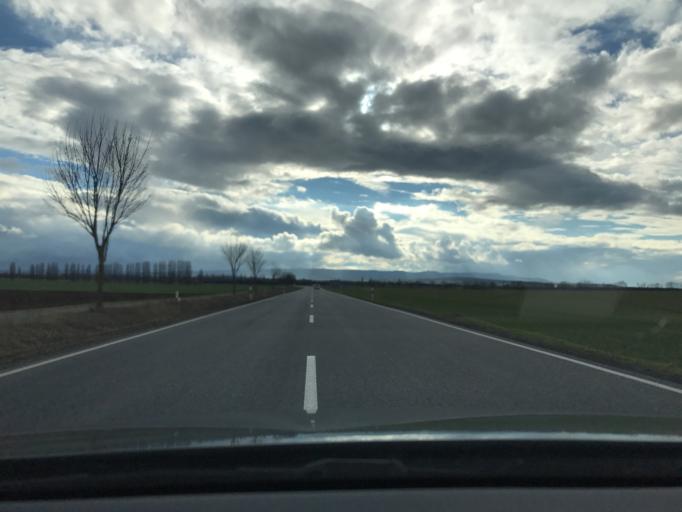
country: DE
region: Saxony-Anhalt
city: Sangerhausen
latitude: 51.4653
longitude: 11.2608
